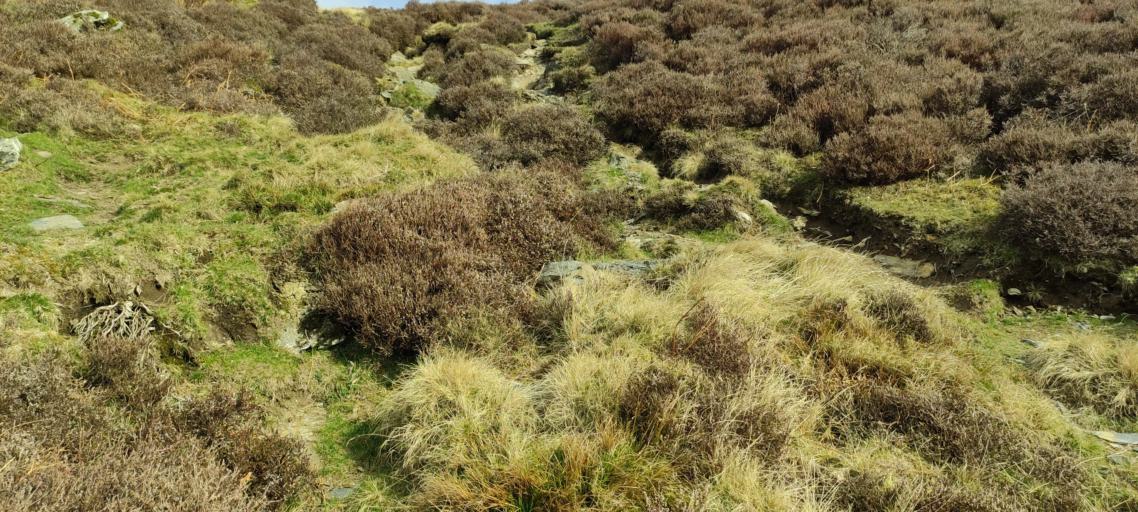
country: GB
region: England
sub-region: Cumbria
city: Keswick
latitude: 54.6297
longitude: -3.0454
